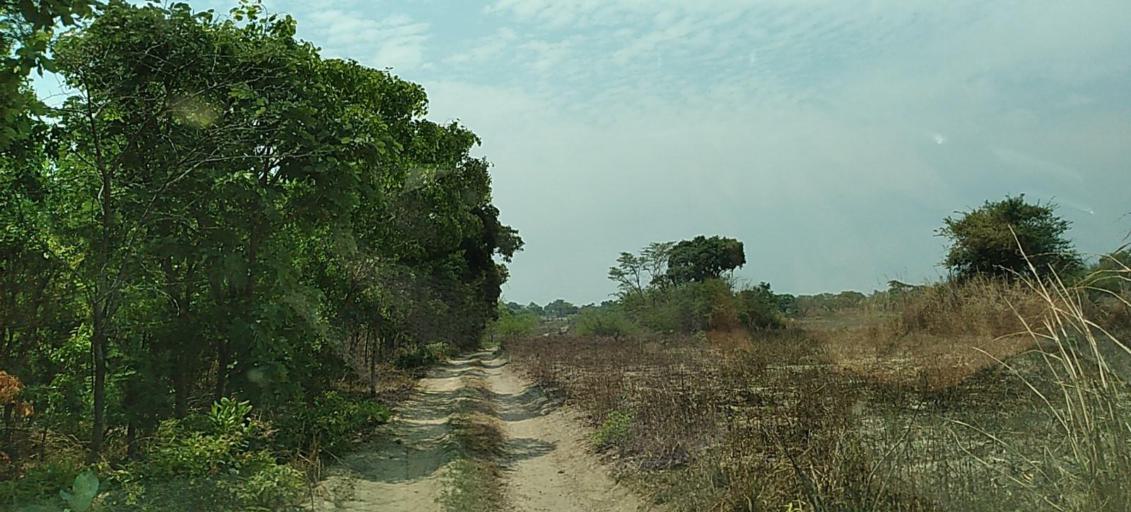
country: ZM
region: Copperbelt
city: Kalulushi
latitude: -12.9333
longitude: 28.1120
